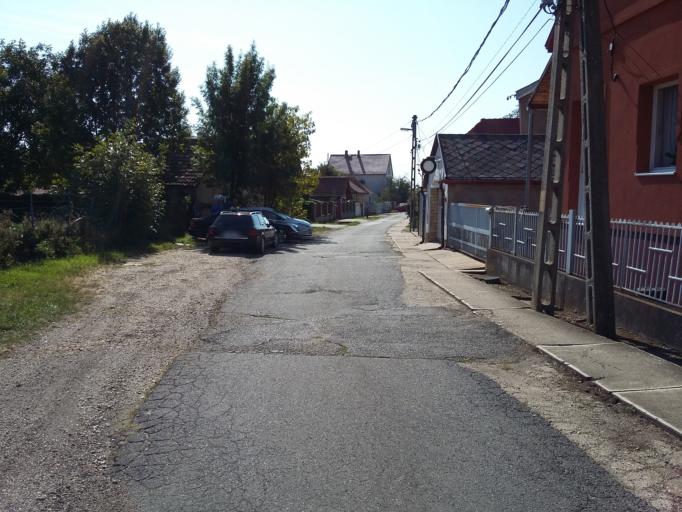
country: HU
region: Borsod-Abauj-Zemplen
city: Bekecs
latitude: 48.1512
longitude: 21.1731
